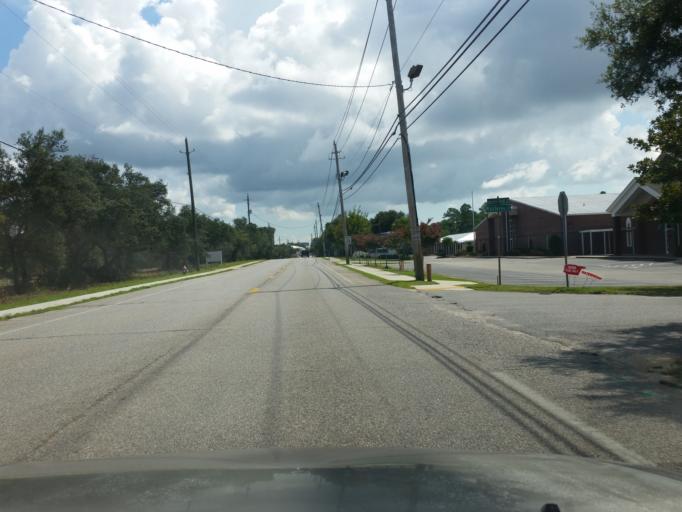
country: US
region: Alabama
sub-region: Baldwin County
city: Orange Beach
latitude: 30.3175
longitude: -87.4327
